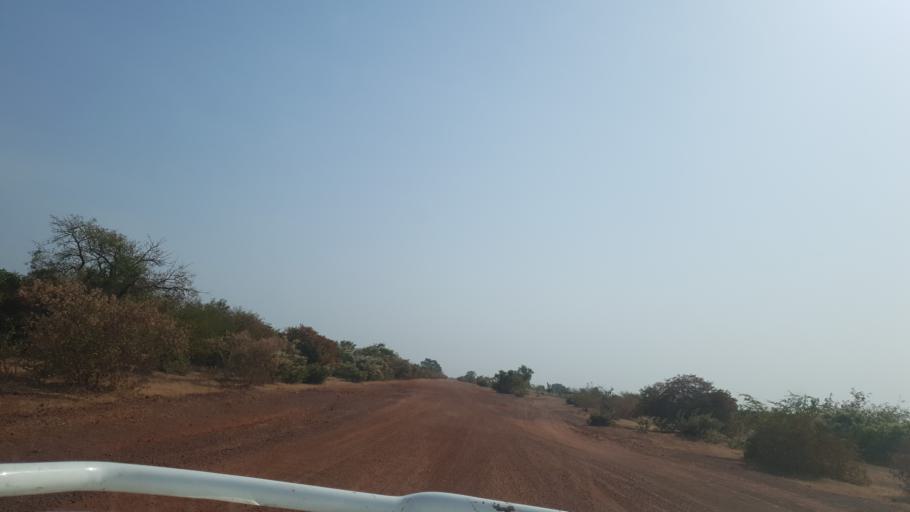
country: ML
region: Koulikoro
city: Dioila
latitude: 12.6696
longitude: -6.6613
